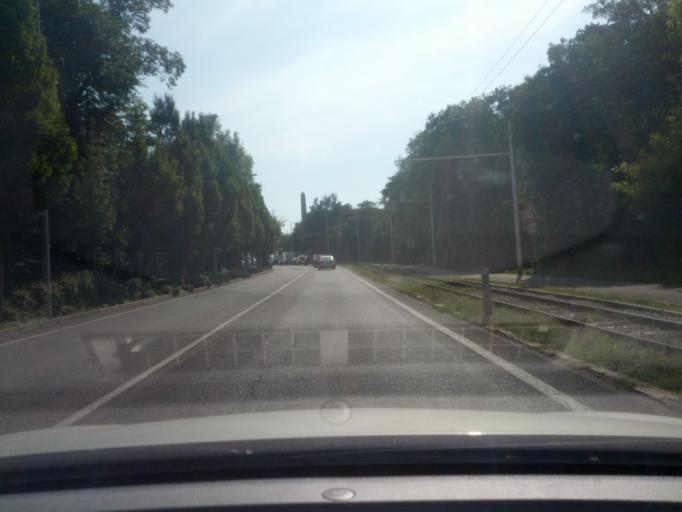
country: IT
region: Friuli Venezia Giulia
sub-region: Provincia di Trieste
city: Villa Opicina
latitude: 45.6814
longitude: 13.7820
